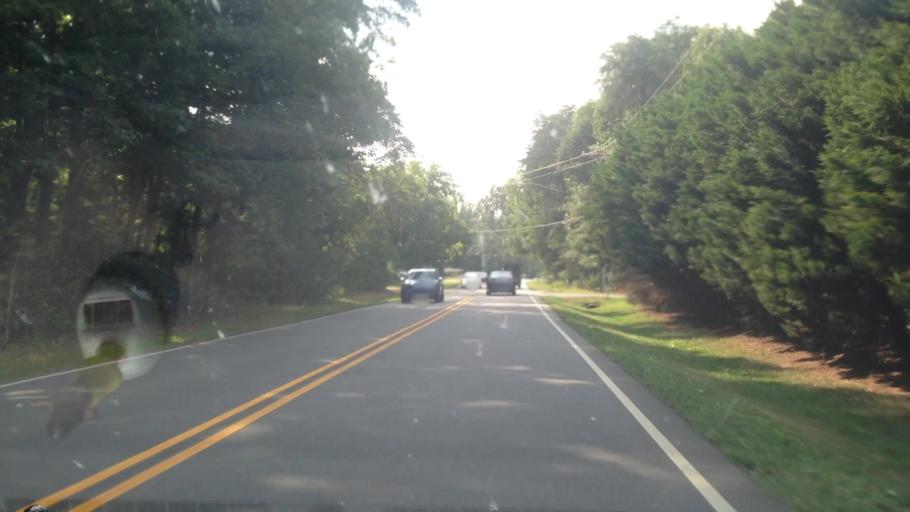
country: US
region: North Carolina
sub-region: Forsyth County
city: Kernersville
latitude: 36.1226
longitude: -80.1093
